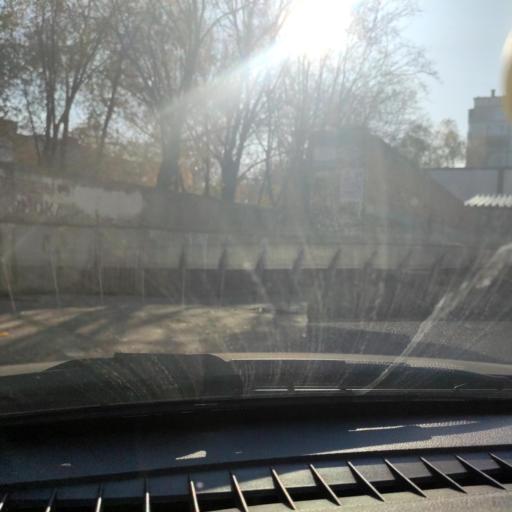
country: RU
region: Samara
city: Tol'yatti
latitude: 53.5195
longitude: 49.2607
